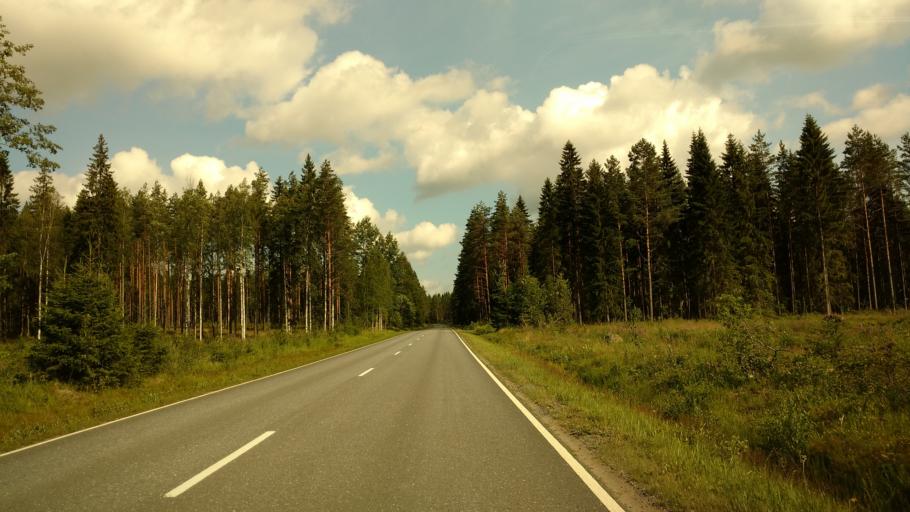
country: FI
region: Varsinais-Suomi
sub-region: Loimaa
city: Koski Tl
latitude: 60.6088
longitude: 23.1214
